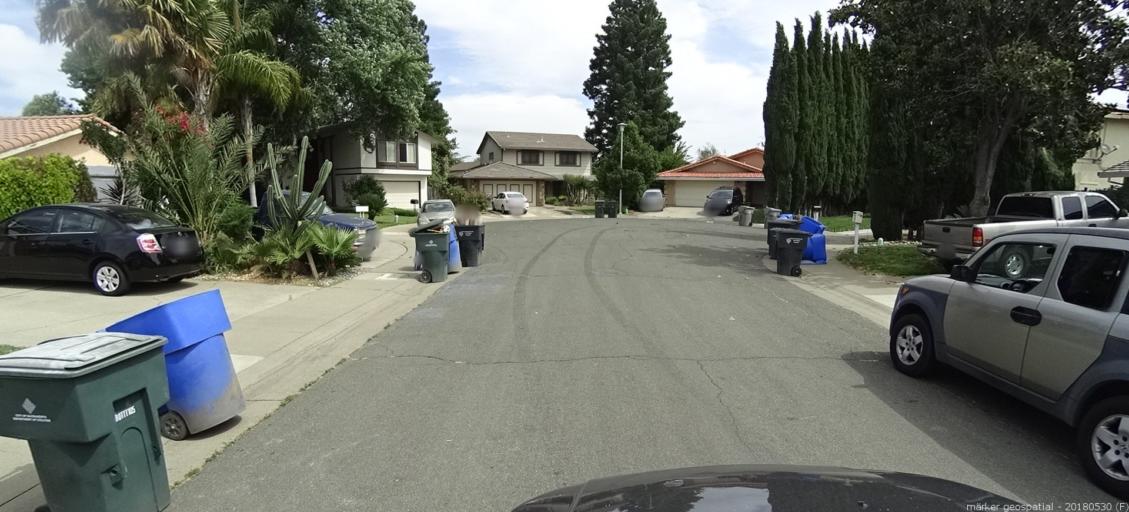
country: US
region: California
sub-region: Sacramento County
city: Sacramento
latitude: 38.6209
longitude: -121.4819
